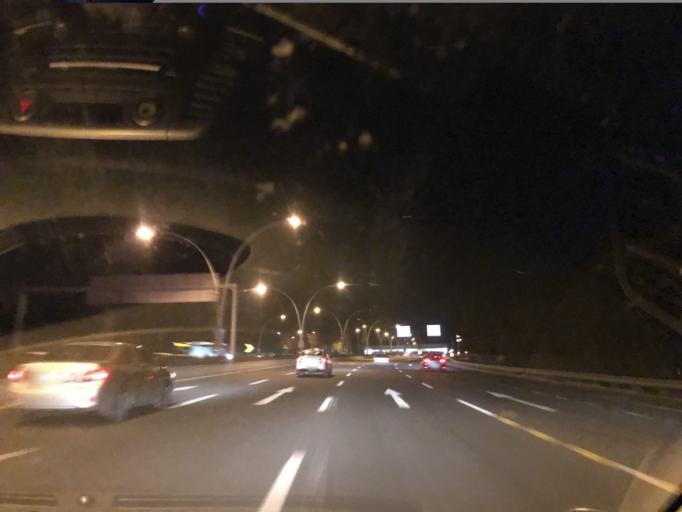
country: TR
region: Ankara
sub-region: Goelbasi
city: Golbasi
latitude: 39.8457
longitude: 32.8094
